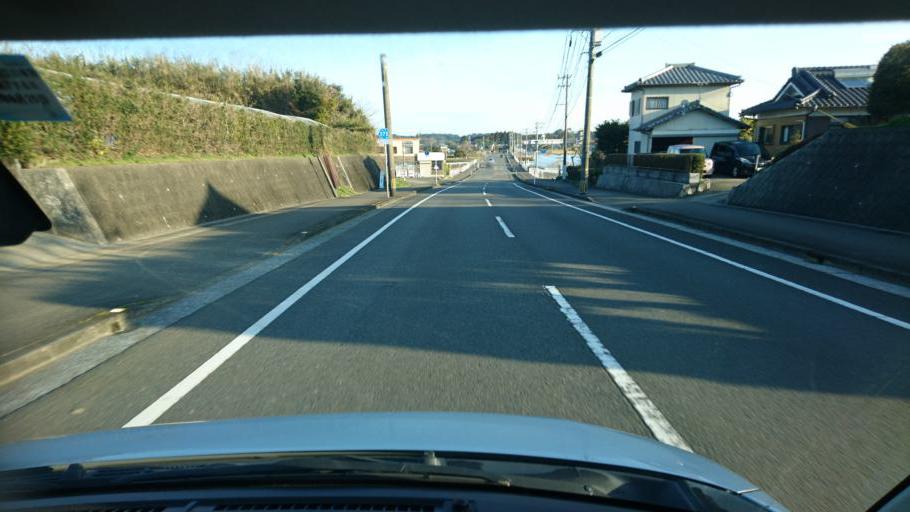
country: JP
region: Miyazaki
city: Miyazaki-shi
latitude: 31.8362
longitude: 131.4197
